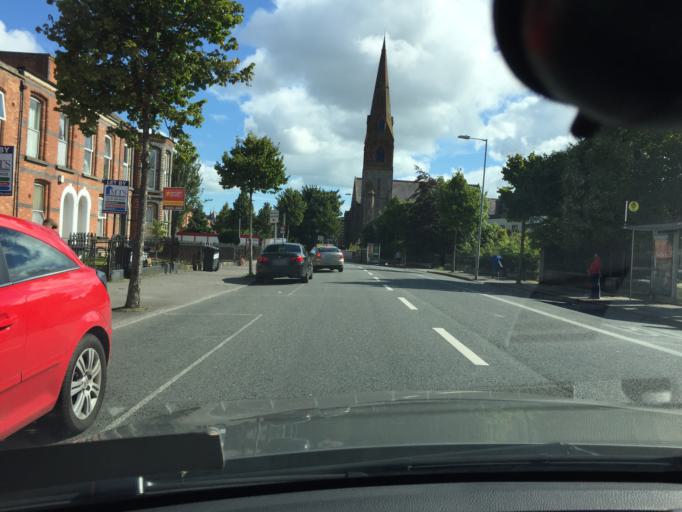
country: IE
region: Leinster
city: Rathmines
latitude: 53.3322
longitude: -6.2734
